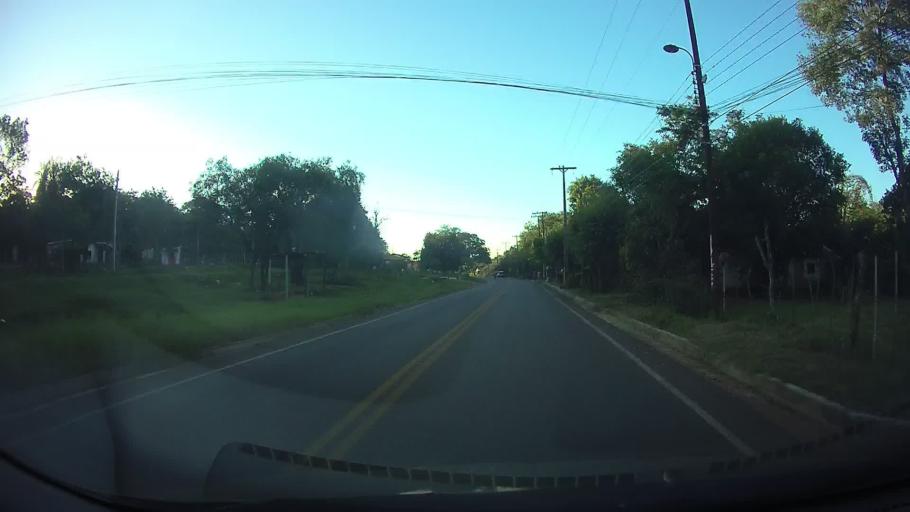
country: PY
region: Central
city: Aregua
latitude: -25.2563
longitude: -57.4554
